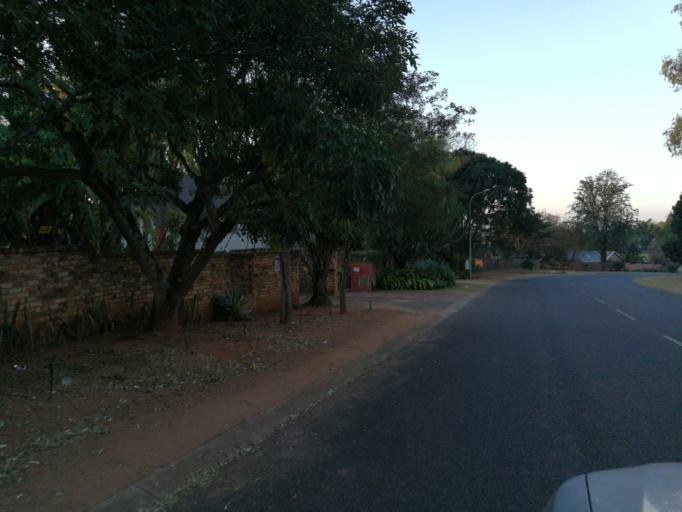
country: ZA
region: Mpumalanga
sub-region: Ehlanzeni District
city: White River
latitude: -25.3197
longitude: 31.0196
